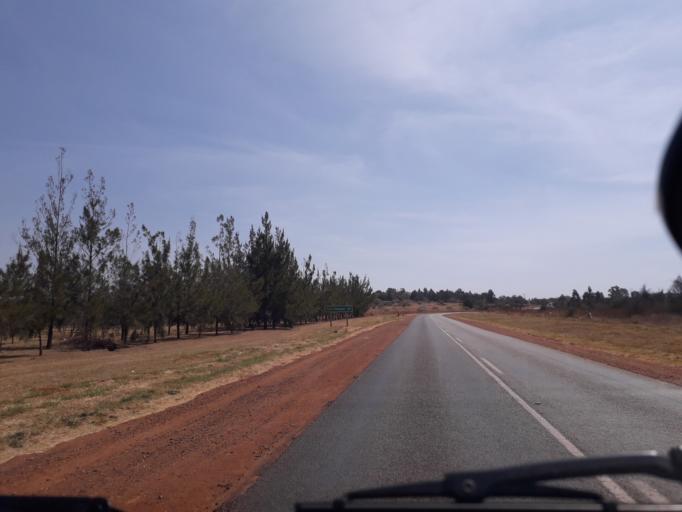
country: ZA
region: Gauteng
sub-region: West Rand District Municipality
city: Krugersdorp
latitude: -26.0026
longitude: 27.7038
